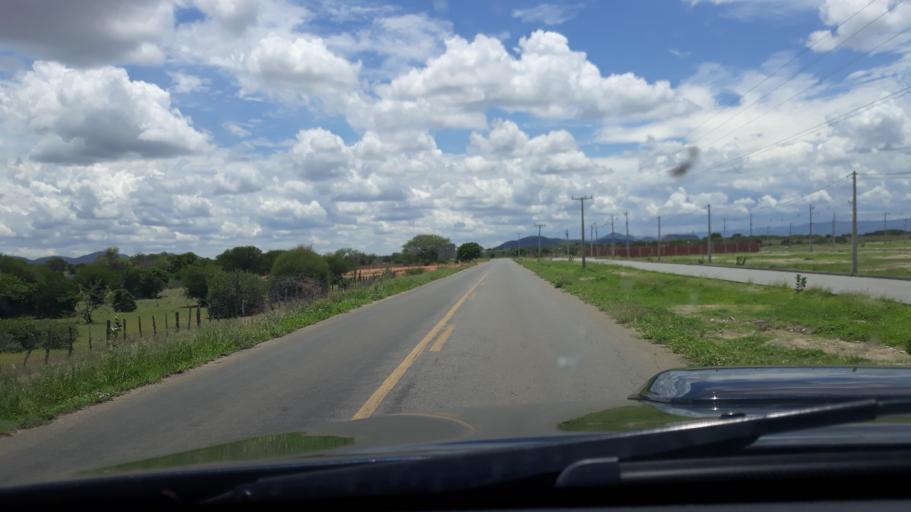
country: BR
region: Bahia
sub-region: Guanambi
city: Guanambi
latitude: -14.1839
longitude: -42.7987
